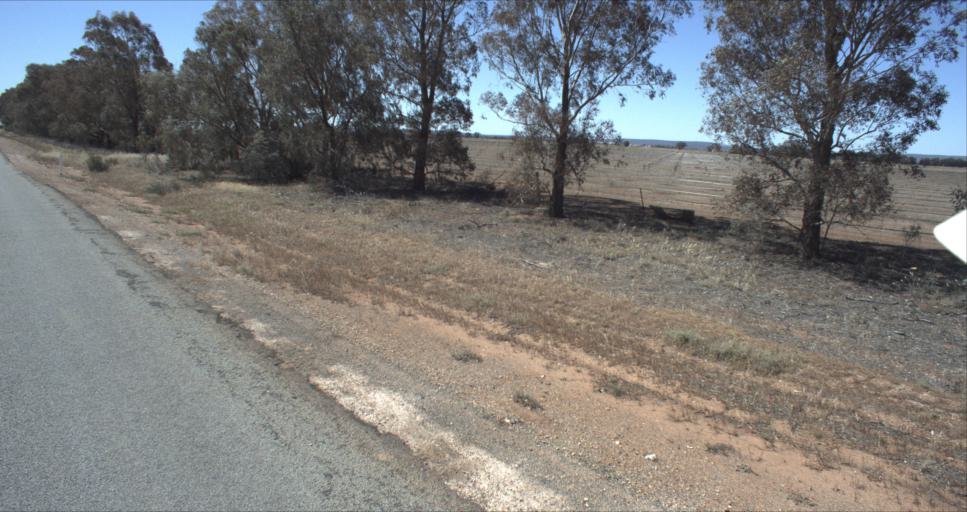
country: AU
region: New South Wales
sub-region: Leeton
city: Leeton
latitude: -34.5148
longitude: 146.3451
